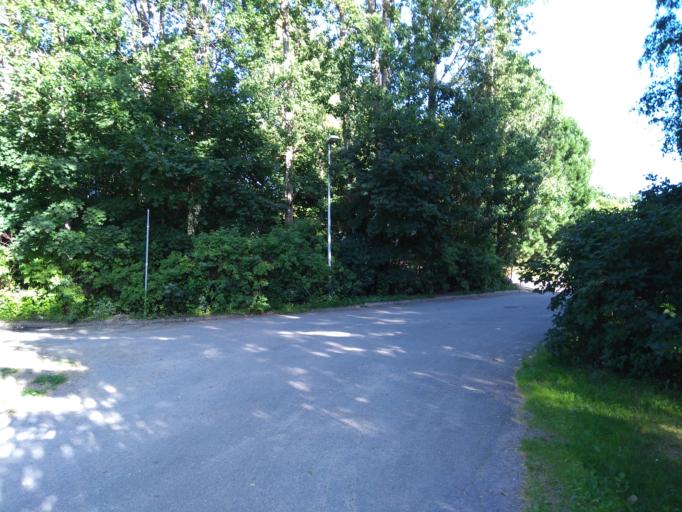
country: FI
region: Uusimaa
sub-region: Helsinki
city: Vantaa
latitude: 60.2605
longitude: 24.9923
